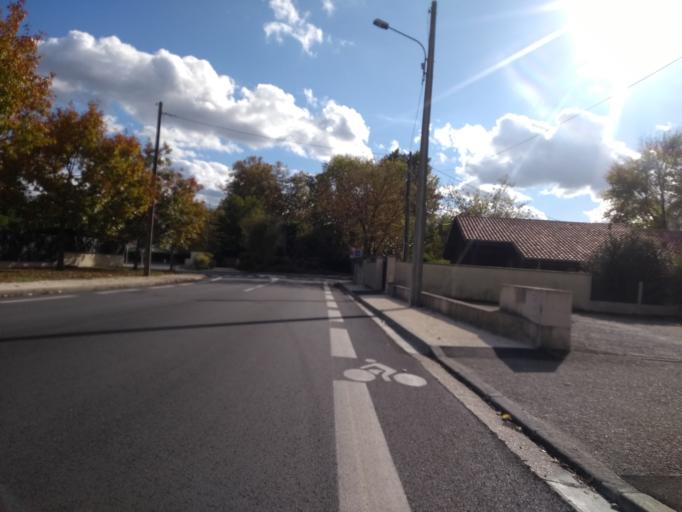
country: FR
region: Aquitaine
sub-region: Departement de la Gironde
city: Gradignan
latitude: 44.7777
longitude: -0.5931
